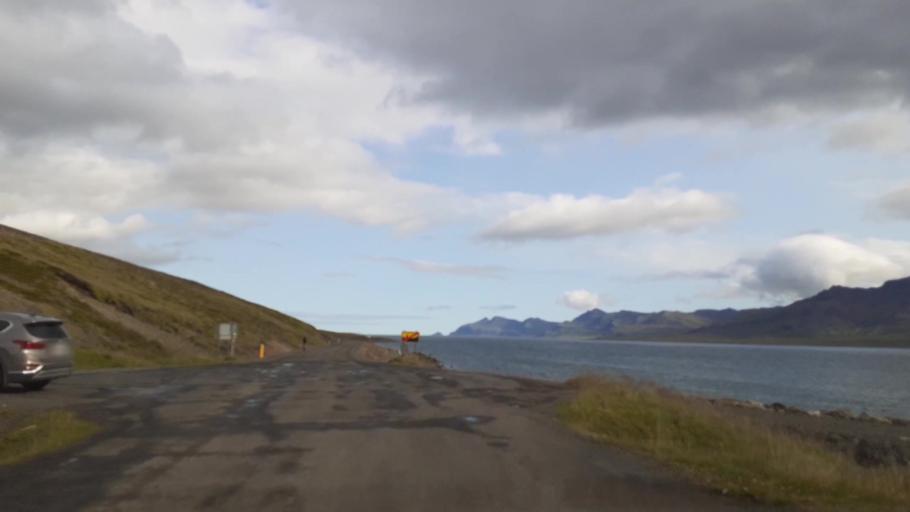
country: IS
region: East
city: Eskifjoerdur
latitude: 65.0599
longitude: -13.9906
